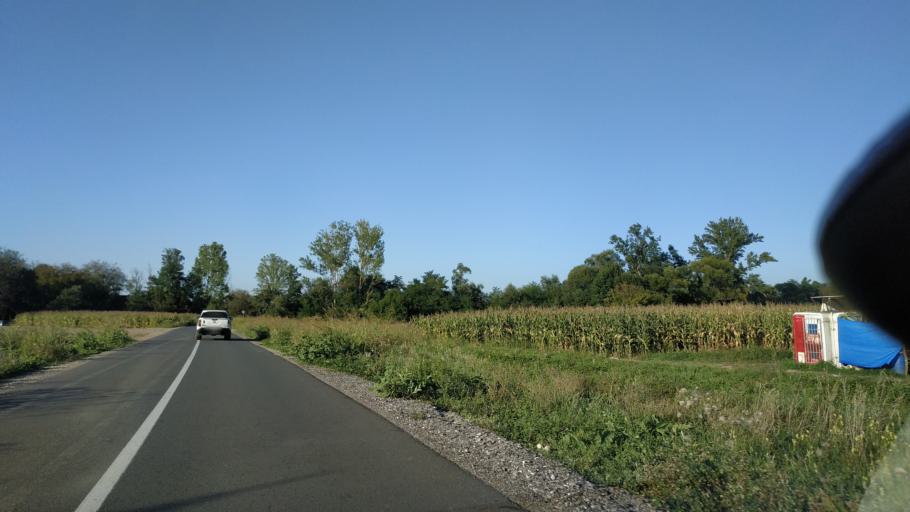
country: RS
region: Central Serbia
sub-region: Rasinski Okrug
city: Krusevac
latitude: 43.5289
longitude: 21.3404
